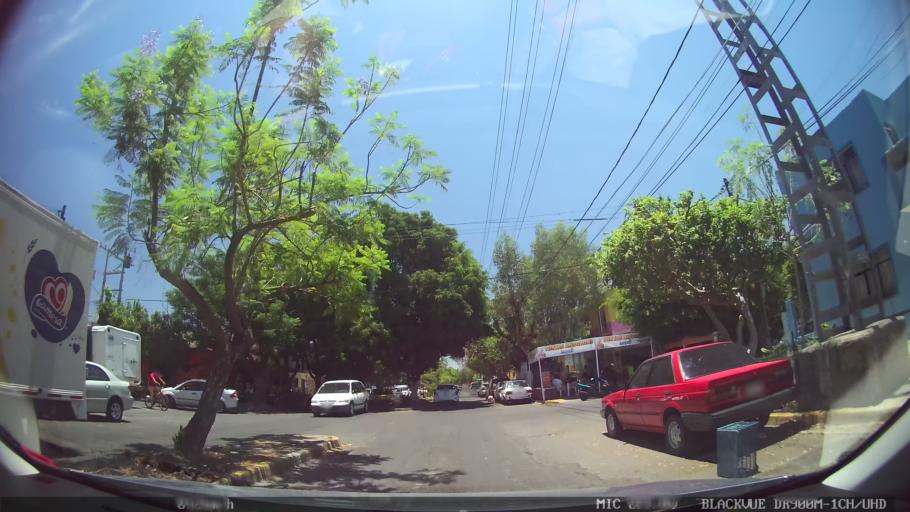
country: MX
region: Jalisco
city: Tlaquepaque
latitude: 20.6673
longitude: -103.2851
